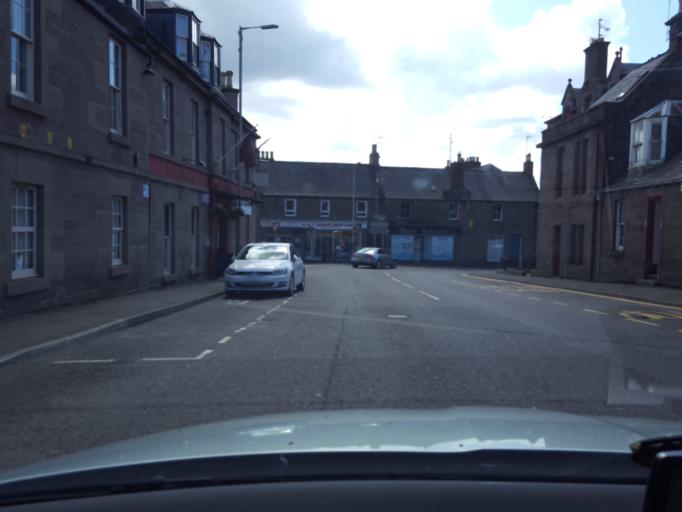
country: GB
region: Scotland
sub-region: Angus
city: Brechin
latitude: 56.7331
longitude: -2.6593
